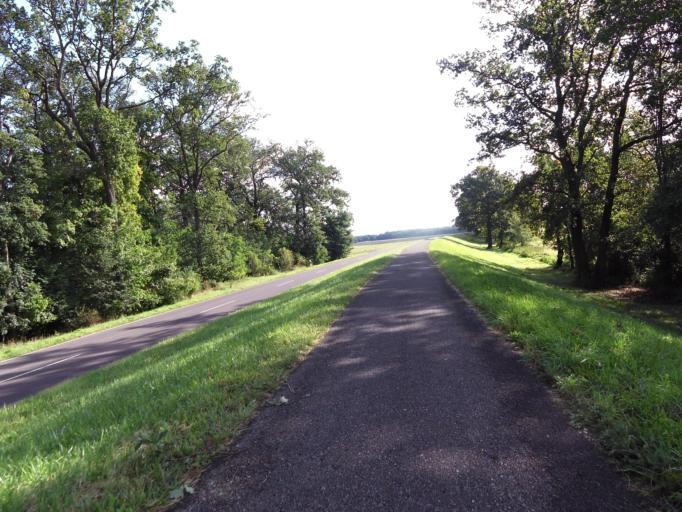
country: DE
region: Saxony-Anhalt
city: Plotzky
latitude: 52.0346
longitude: 11.7860
